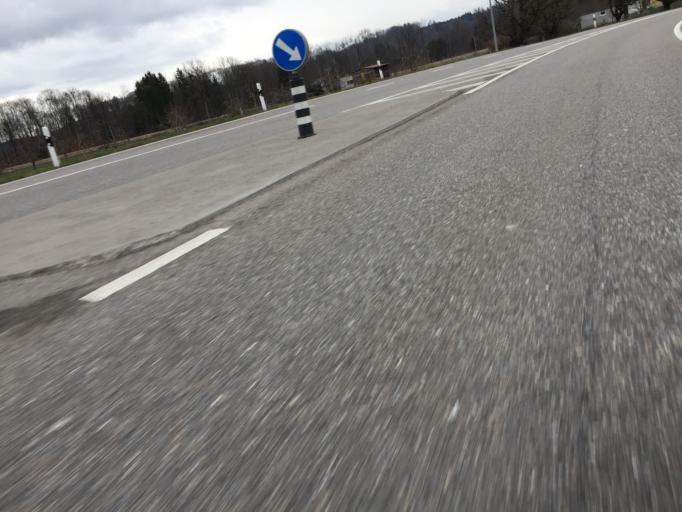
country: CH
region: Bern
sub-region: Emmental District
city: Kirchberg
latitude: 47.0757
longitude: 7.5844
